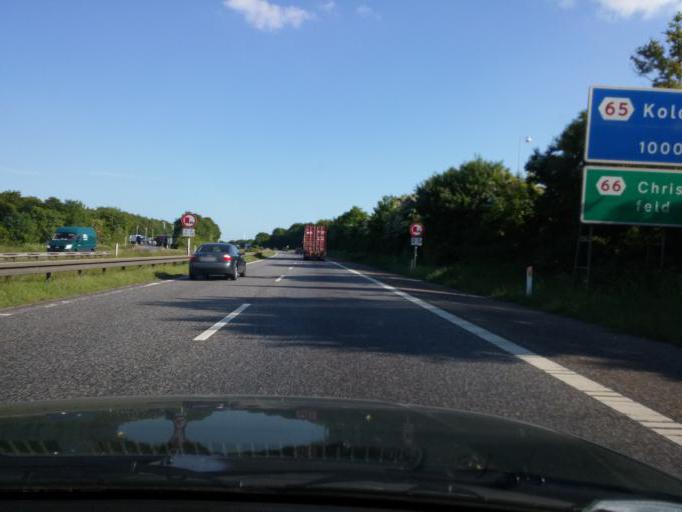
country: DK
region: South Denmark
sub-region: Kolding Kommune
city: Kolding
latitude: 55.4769
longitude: 9.4242
